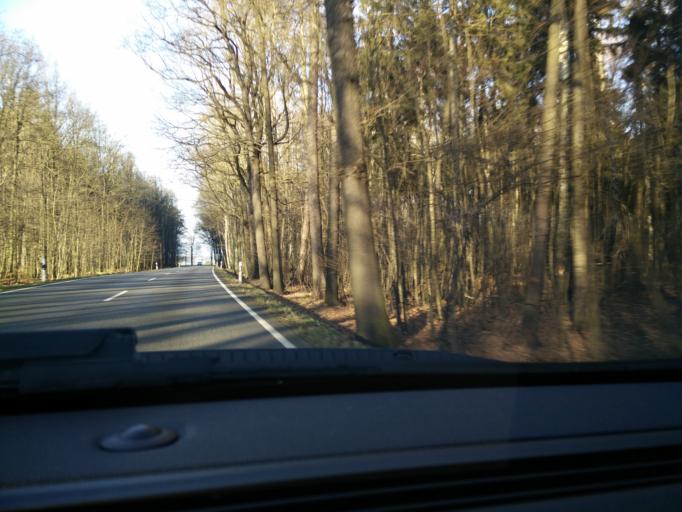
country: DE
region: Saxony
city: Konigsfeld
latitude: 51.0787
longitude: 12.7216
